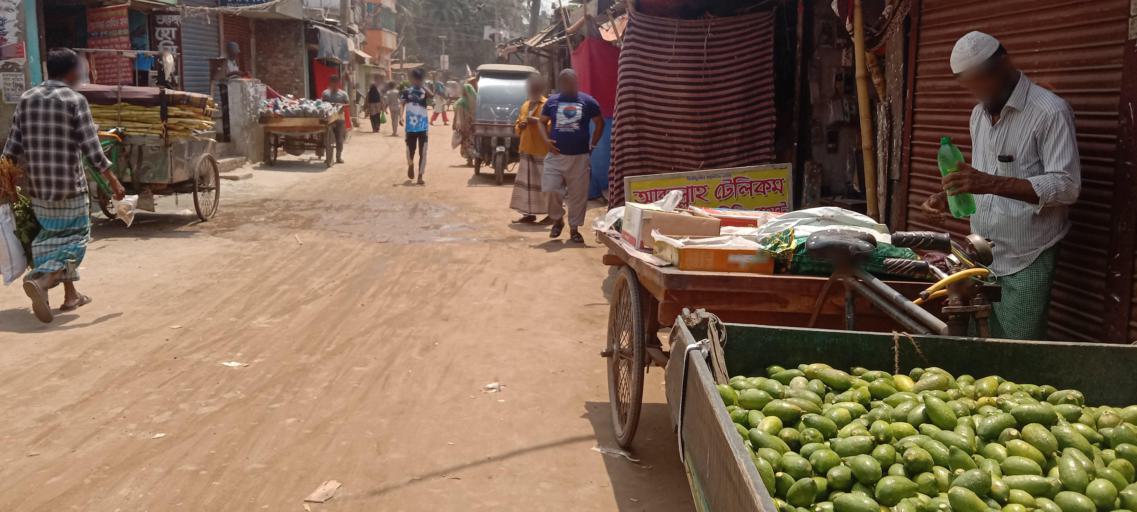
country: BD
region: Dhaka
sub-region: Dhaka
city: Dhaka
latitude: 23.6811
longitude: 90.4198
